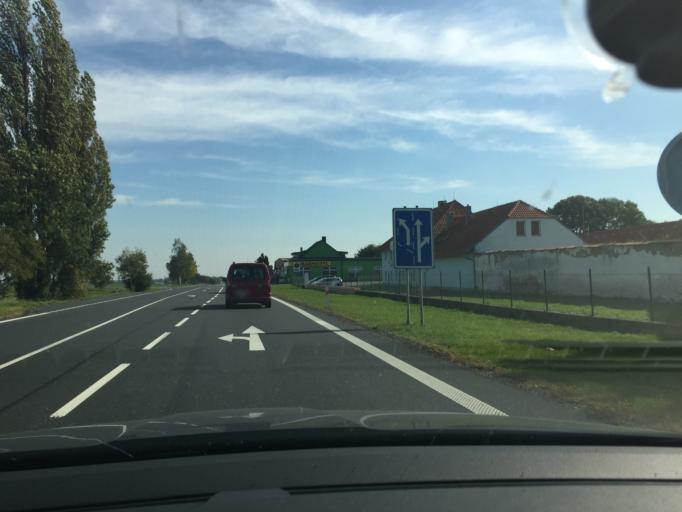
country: CZ
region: Central Bohemia
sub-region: Okres Kolin
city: Kourim
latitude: 50.0489
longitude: 14.9660
